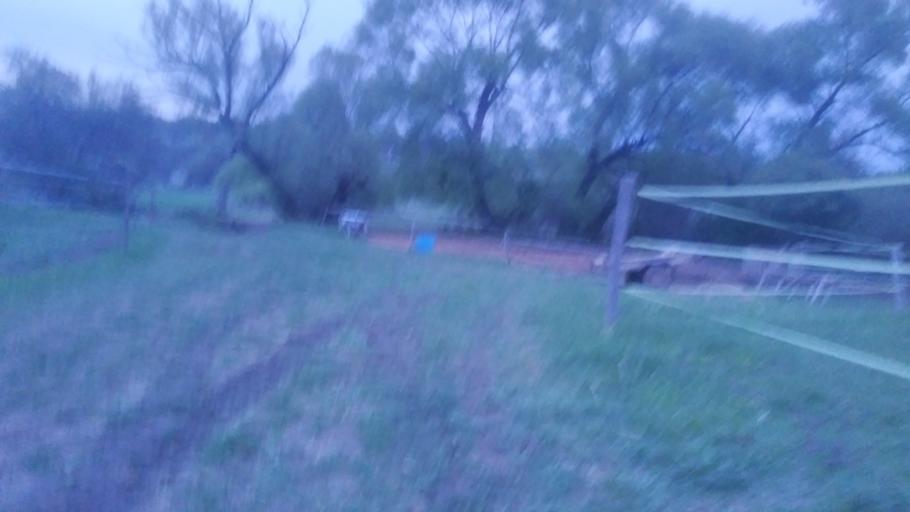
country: HU
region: Pest
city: Pomaz
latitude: 47.6291
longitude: 19.0230
